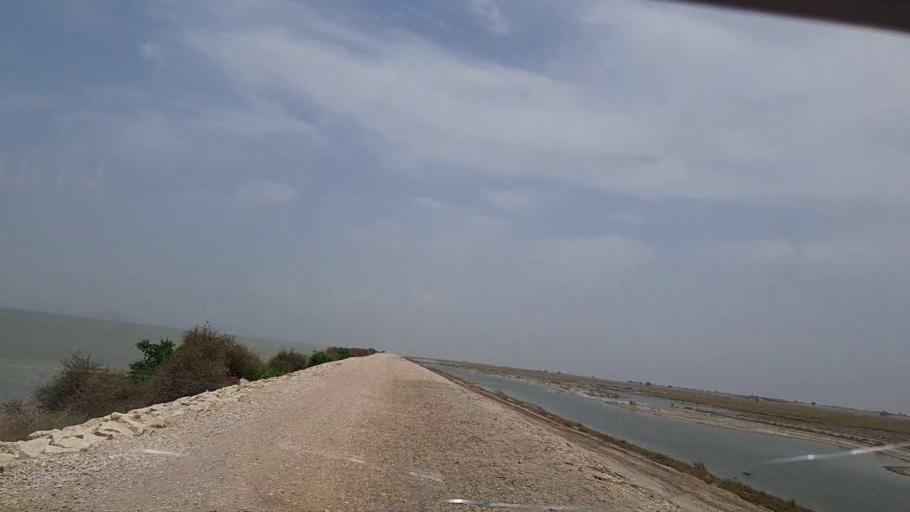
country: PK
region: Sindh
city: Sehwan
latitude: 26.4187
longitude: 67.7386
